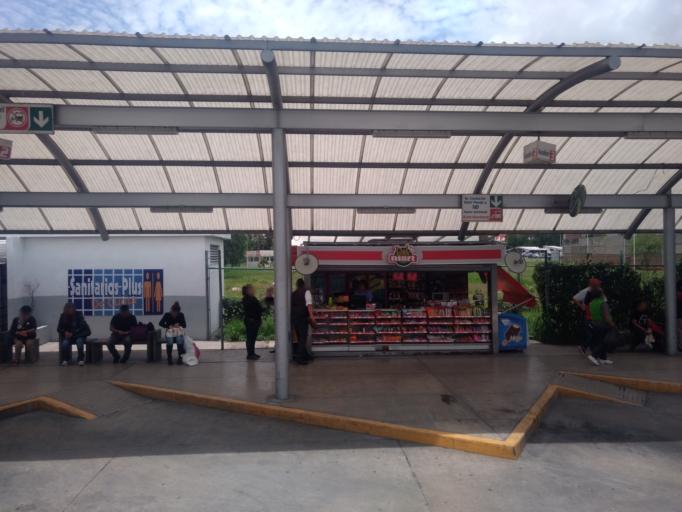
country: MX
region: Puebla
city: Puebla
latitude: 19.0768
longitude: -98.2039
